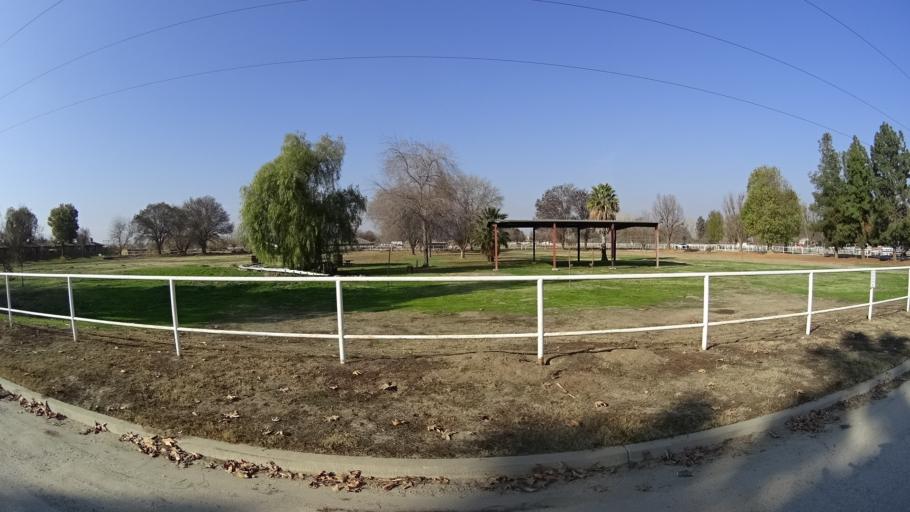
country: US
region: California
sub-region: Kern County
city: Oildale
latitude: 35.4053
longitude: -119.0052
